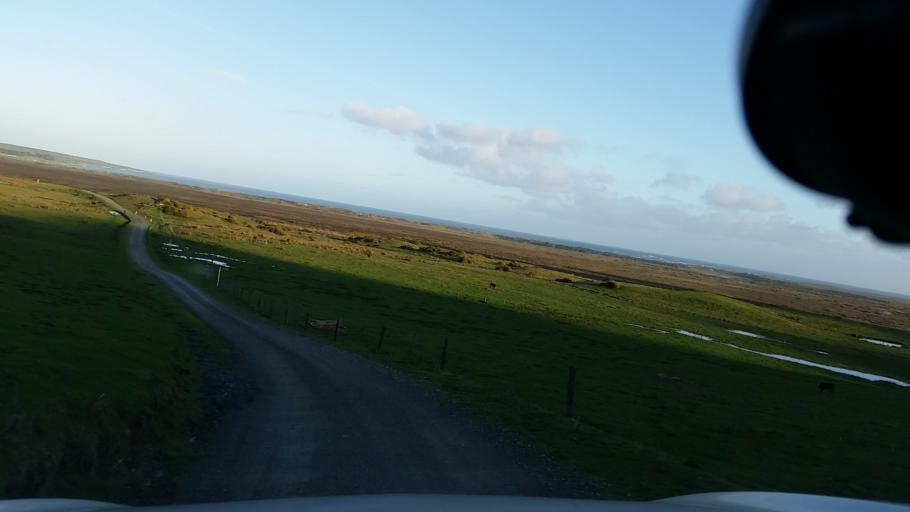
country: NZ
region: Chatham Islands
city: Waitangi
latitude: -43.7751
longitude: -176.7738
